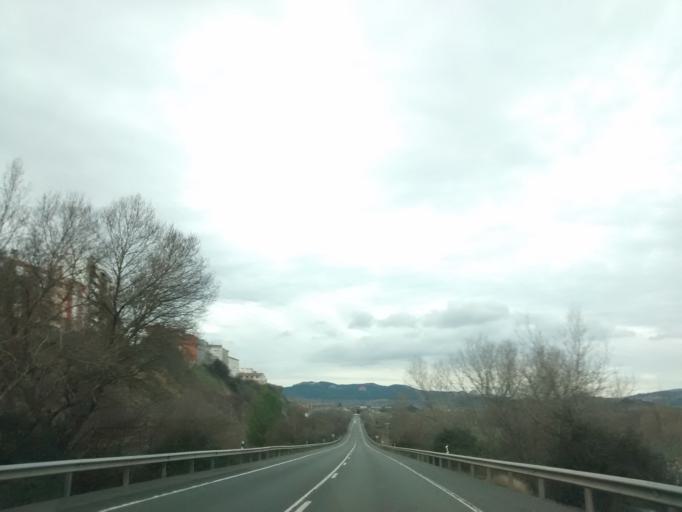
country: ES
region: La Rioja
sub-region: Provincia de La Rioja
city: Haro
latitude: 42.5731
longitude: -2.8397
